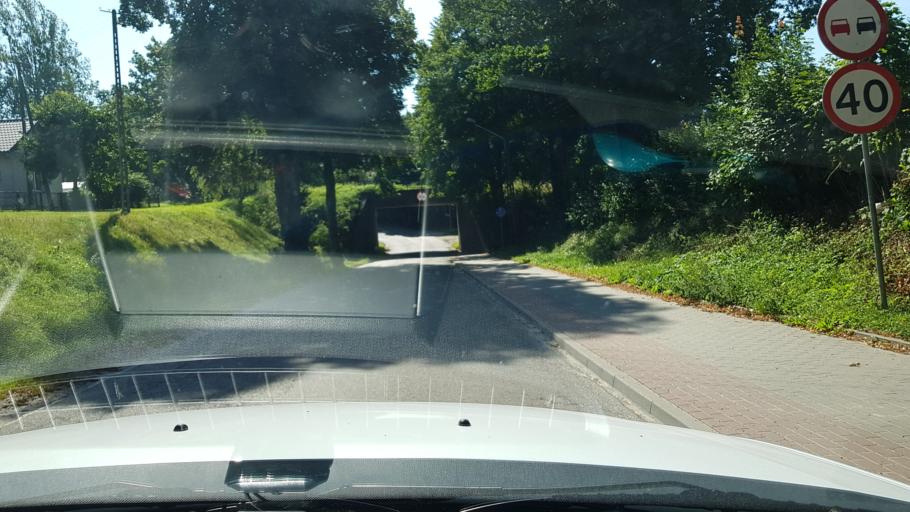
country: PL
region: West Pomeranian Voivodeship
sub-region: Powiat koszalinski
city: Sianow
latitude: 54.2431
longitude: 16.2917
